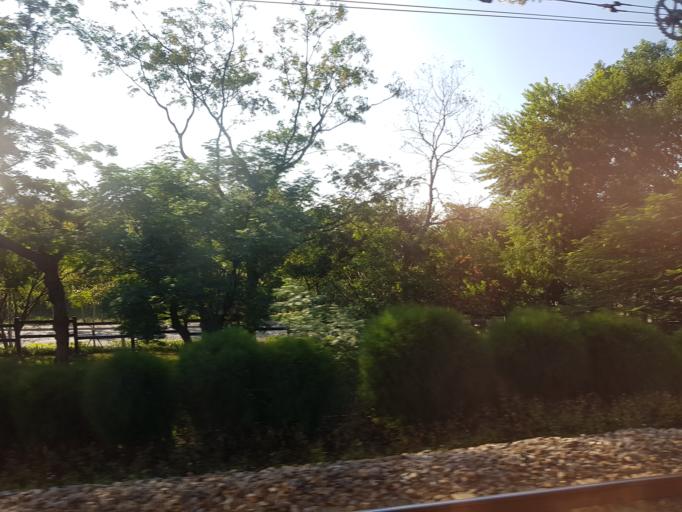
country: TW
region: Taiwan
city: Fengyuan
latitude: 24.2976
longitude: 120.7325
